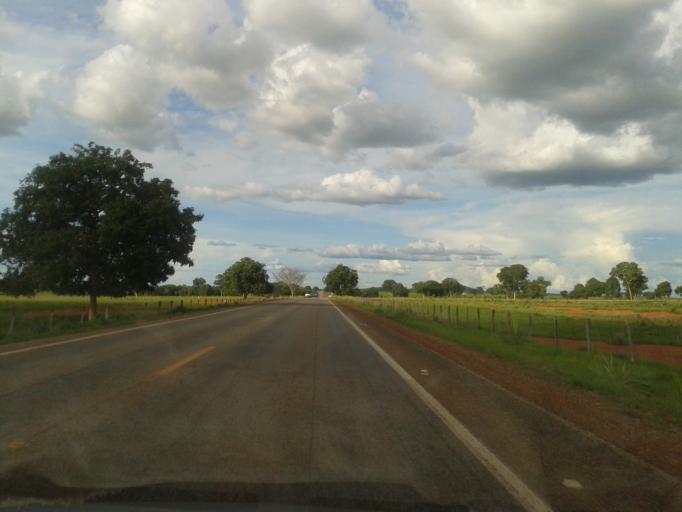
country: BR
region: Goias
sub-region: Crixas
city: Crixas
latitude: -14.1619
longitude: -50.3660
